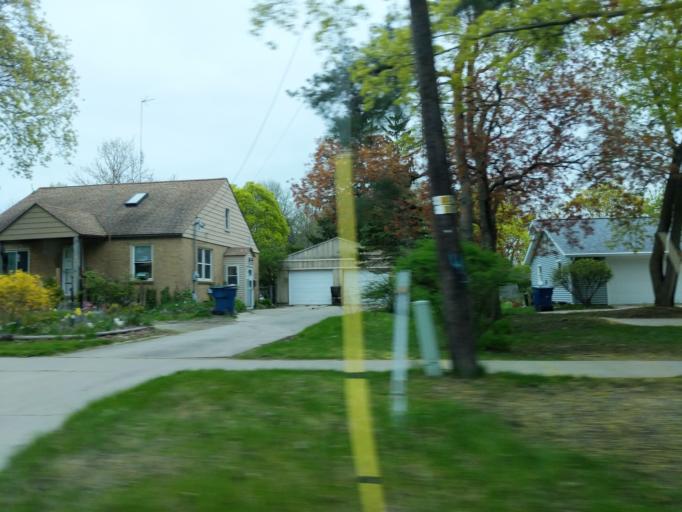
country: US
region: Michigan
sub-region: Midland County
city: Midland
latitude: 43.6330
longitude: -84.2270
